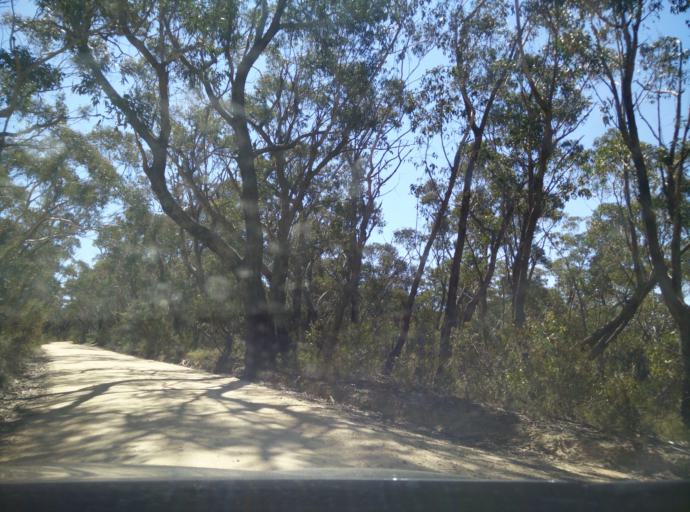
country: AU
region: New South Wales
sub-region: Blue Mountains Municipality
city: Blackheath
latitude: -33.5937
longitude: 150.2668
